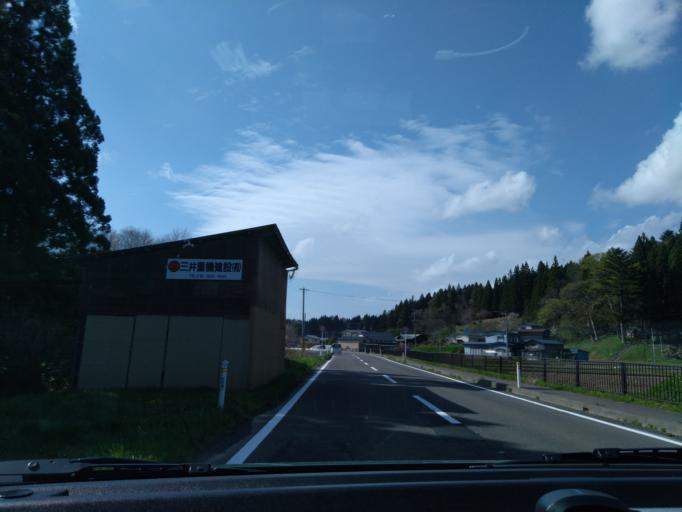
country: JP
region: Akita
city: Akita
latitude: 39.7107
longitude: 140.2041
